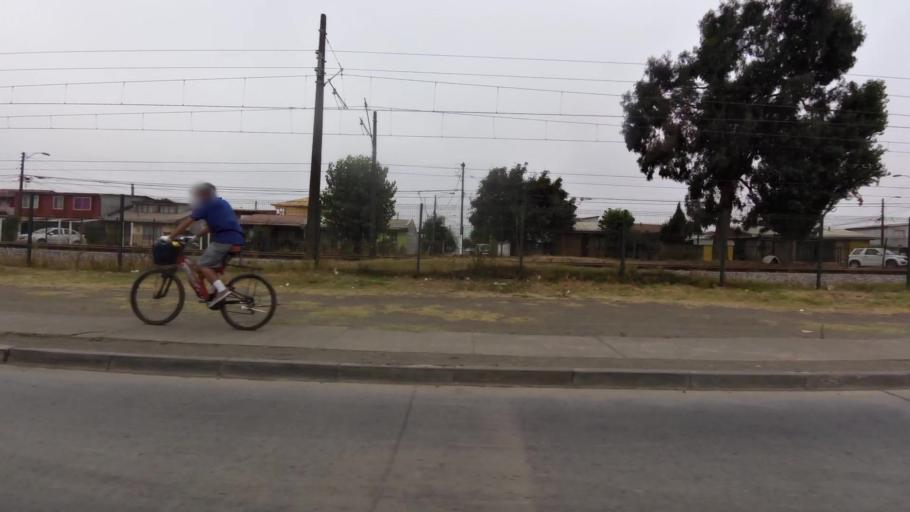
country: CL
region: Biobio
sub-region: Provincia de Concepcion
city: Concepcion
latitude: -36.7986
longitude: -73.0803
